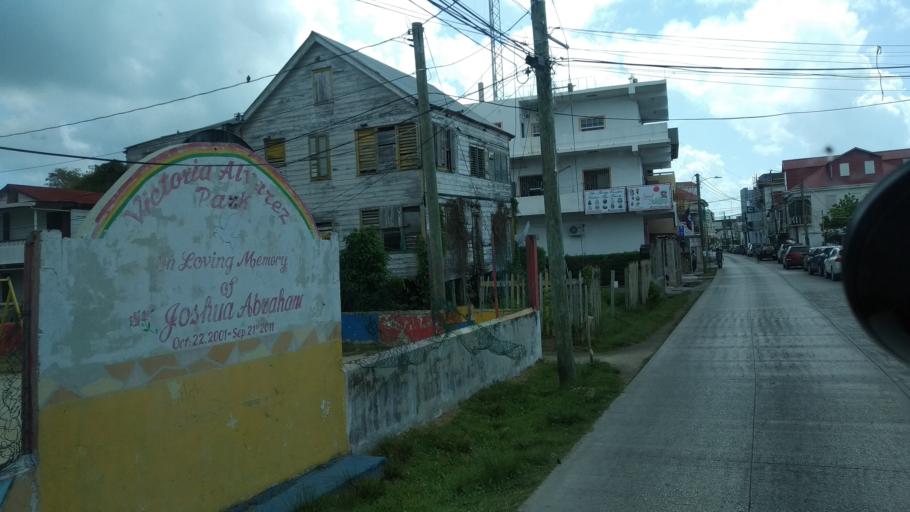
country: BZ
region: Belize
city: Belize City
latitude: 17.4979
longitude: -88.1892
